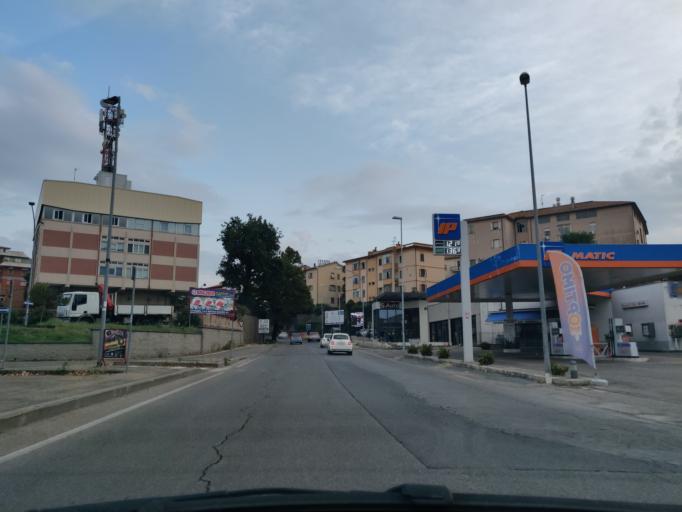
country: IT
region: Latium
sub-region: Provincia di Viterbo
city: Viterbo
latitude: 42.4262
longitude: 12.0991
